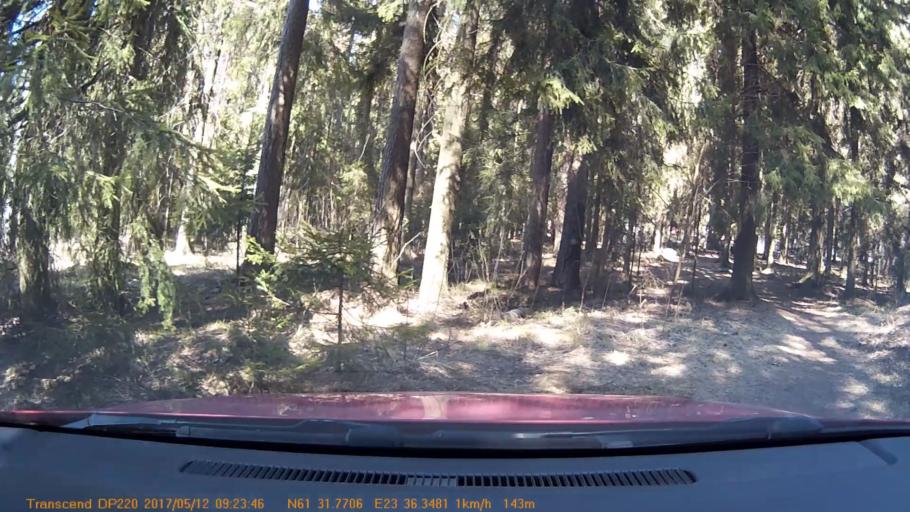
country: FI
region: Pirkanmaa
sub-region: Tampere
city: Yloejaervi
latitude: 61.5295
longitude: 23.6058
